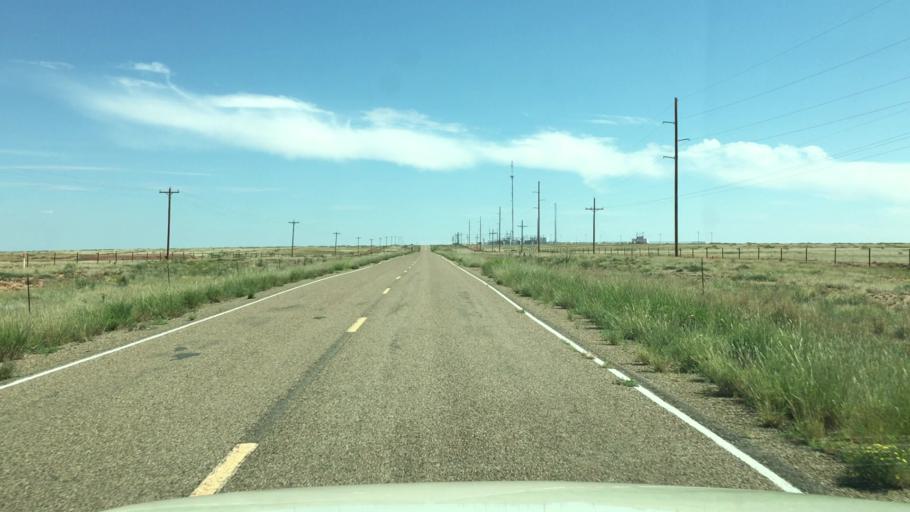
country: US
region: New Mexico
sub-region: Chaves County
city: Roswell
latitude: 33.9571
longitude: -104.5853
